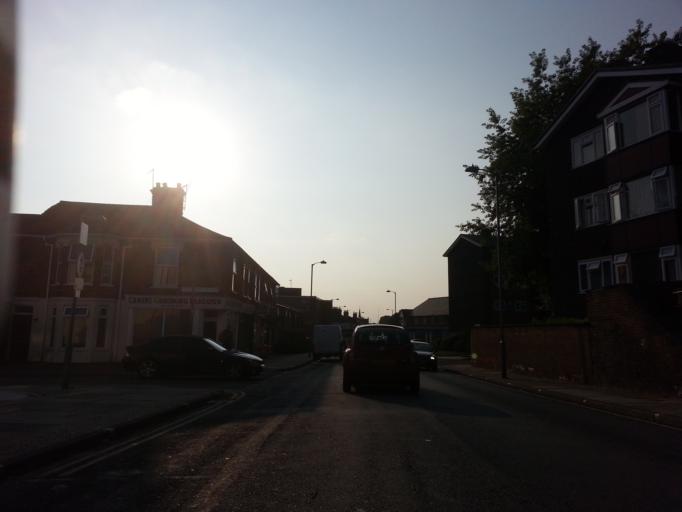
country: GB
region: England
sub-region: Suffolk
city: Ipswich
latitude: 52.0622
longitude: 1.1408
